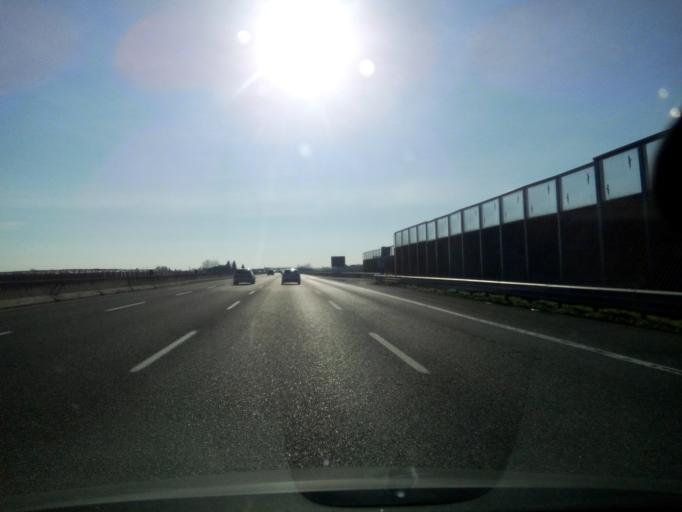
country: IT
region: Emilia-Romagna
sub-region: Provincia di Modena
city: San Vito
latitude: 44.5734
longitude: 11.0022
